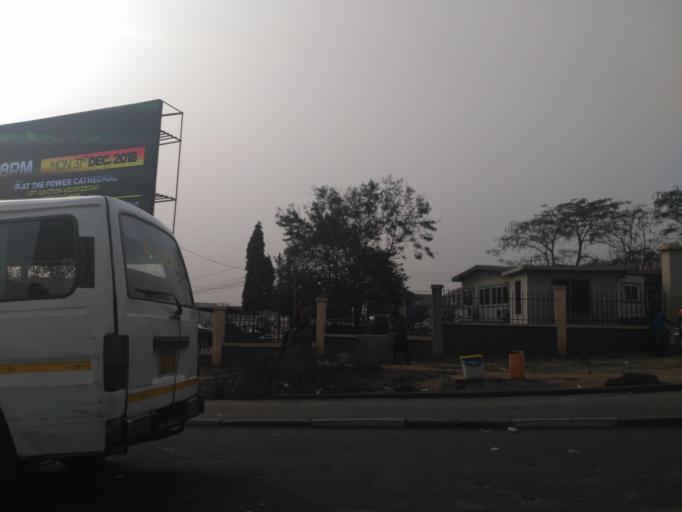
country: GH
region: Ashanti
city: Kumasi
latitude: 6.7117
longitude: -1.6281
